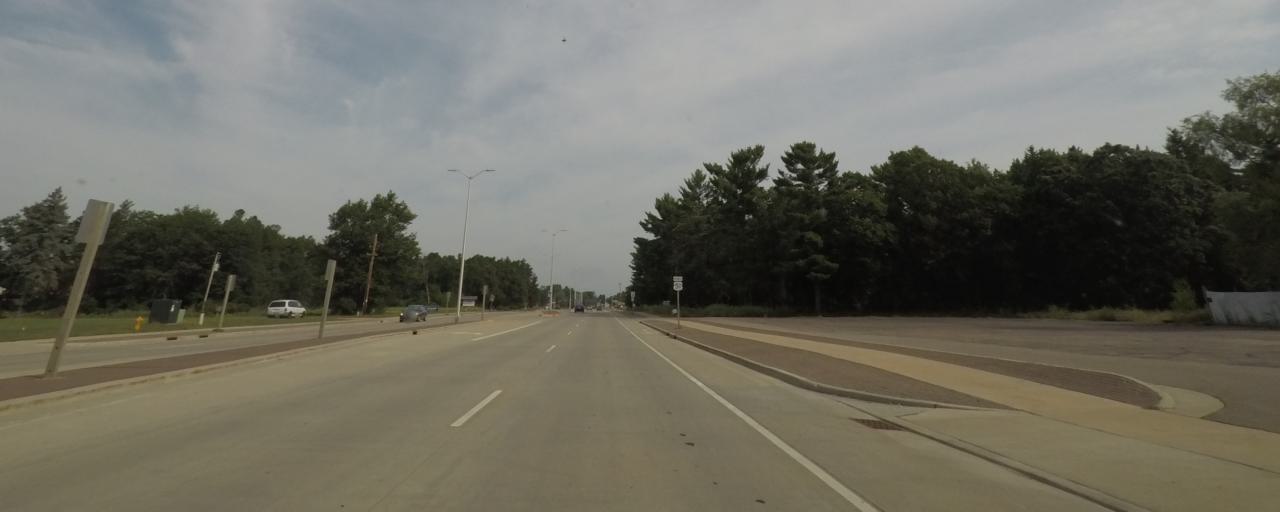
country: US
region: Wisconsin
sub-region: Portage County
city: Plover
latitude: 44.4650
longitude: -89.5449
